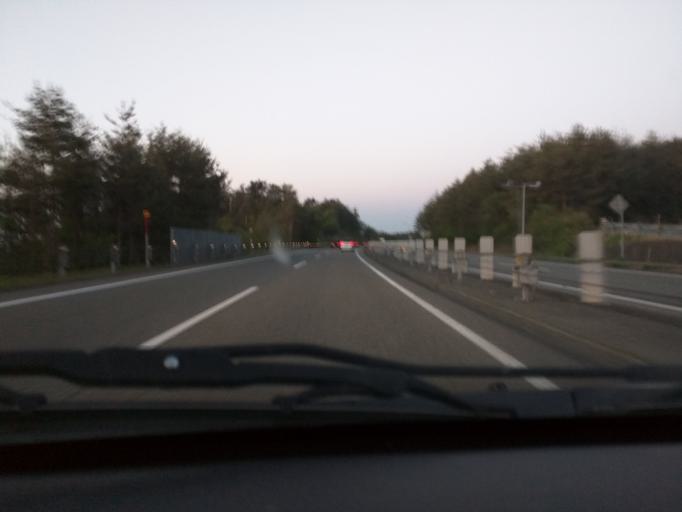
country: JP
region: Niigata
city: Kashiwazaki
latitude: 37.3467
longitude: 138.4947
